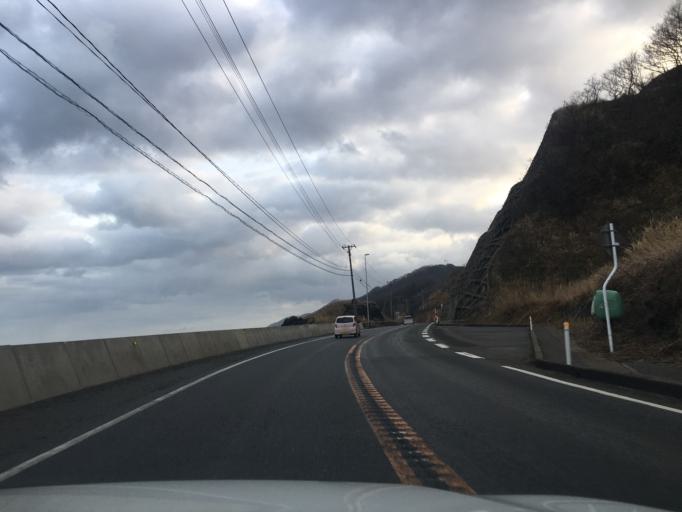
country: JP
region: Yamagata
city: Tsuruoka
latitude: 38.5954
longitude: 139.5649
